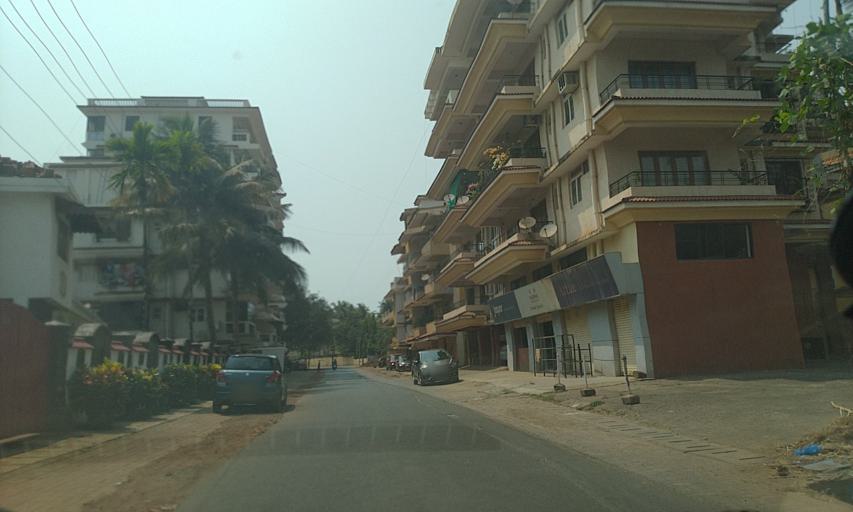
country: IN
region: Goa
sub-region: North Goa
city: Taleigao
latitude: 15.4722
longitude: 73.8105
